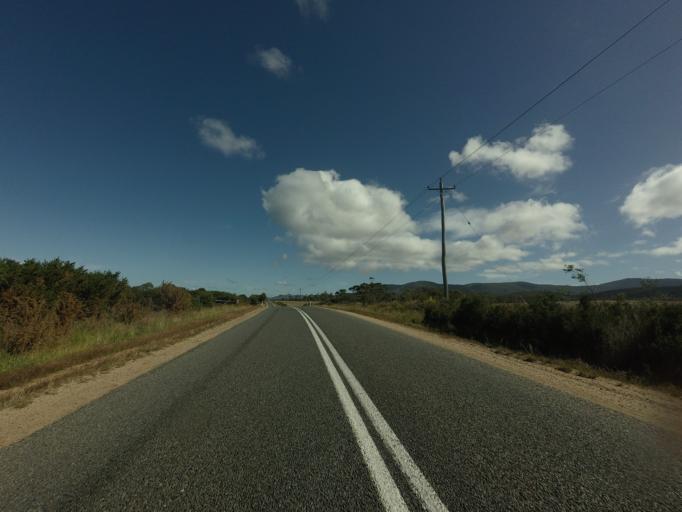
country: AU
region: Tasmania
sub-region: Break O'Day
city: St Helens
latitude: -41.7580
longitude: 148.2736
